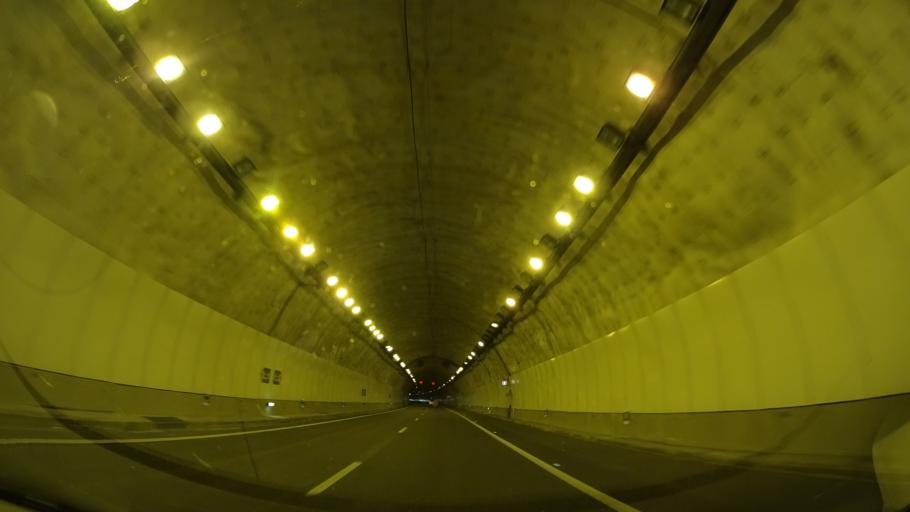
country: ES
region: Andalusia
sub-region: Provincia de Sevilla
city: El Ronquillo
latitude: 37.6446
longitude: -6.1563
